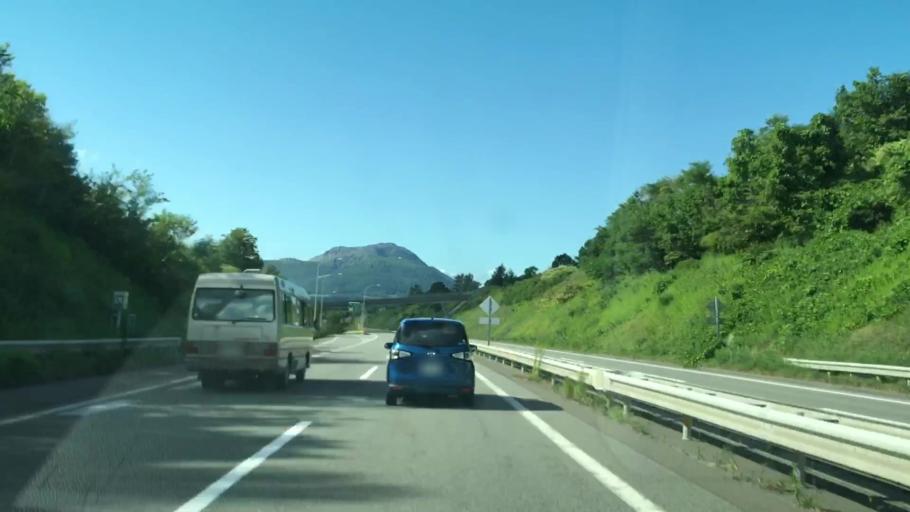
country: JP
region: Hokkaido
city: Date
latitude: 42.4790
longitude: 140.8999
